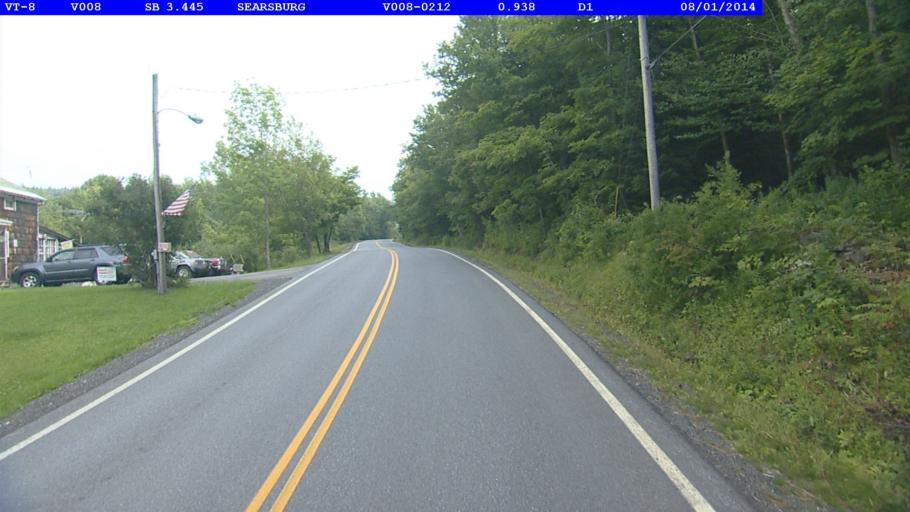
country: US
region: Vermont
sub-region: Windham County
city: Dover
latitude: 42.8709
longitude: -72.9709
